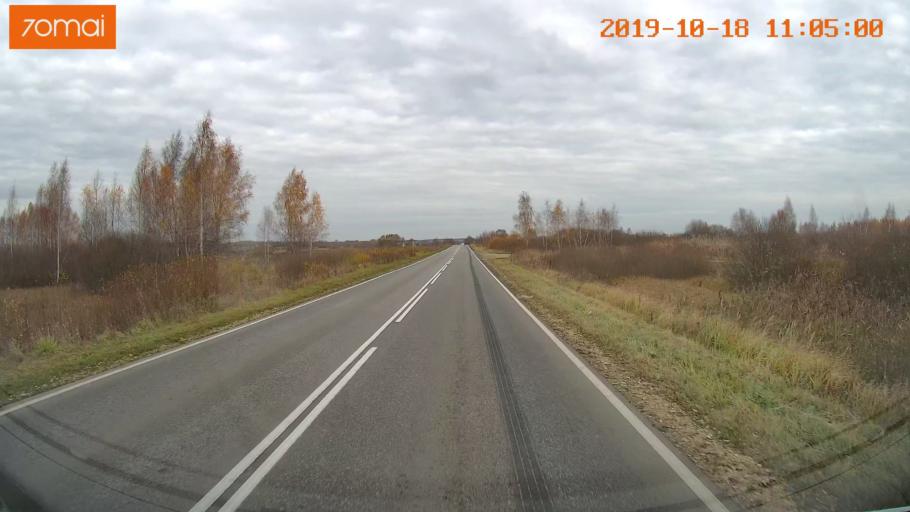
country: RU
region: Tula
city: Kimovsk
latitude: 53.9002
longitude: 38.5415
